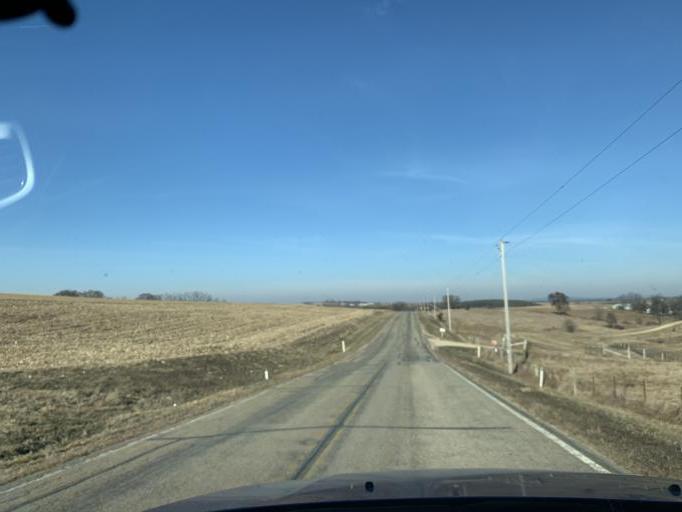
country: US
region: Wisconsin
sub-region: Iowa County
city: Barneveld
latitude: 42.8314
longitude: -89.9314
